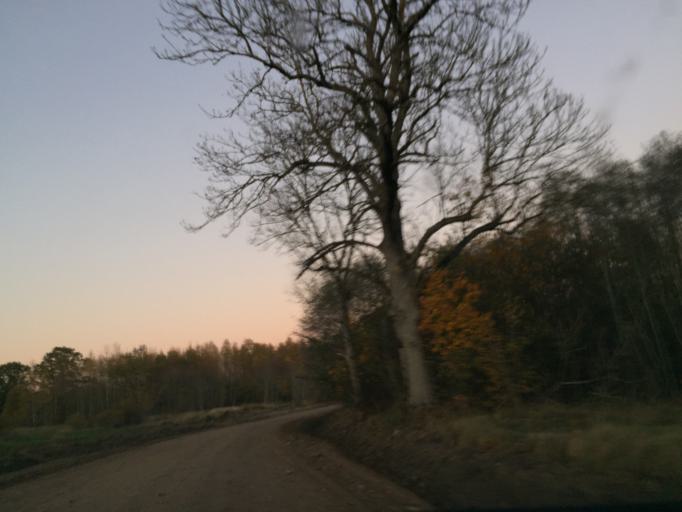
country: LV
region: Auces Novads
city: Auce
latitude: 56.4092
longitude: 22.7996
